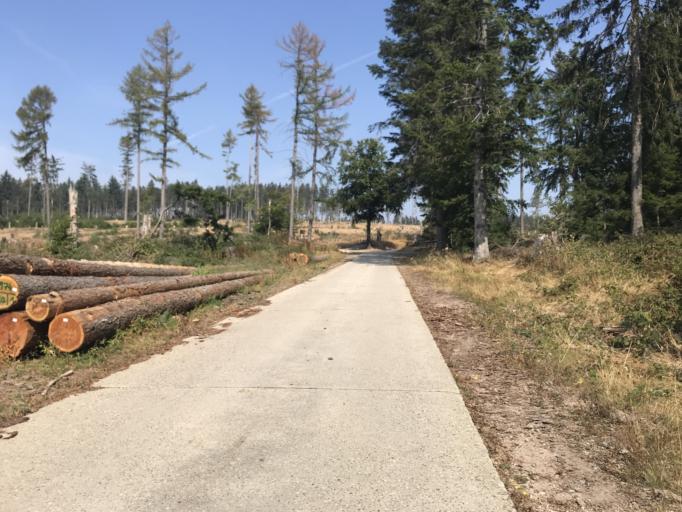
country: DE
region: Rheinland-Pfalz
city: Oestrich-Winkel
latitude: 50.0502
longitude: 8.0073
